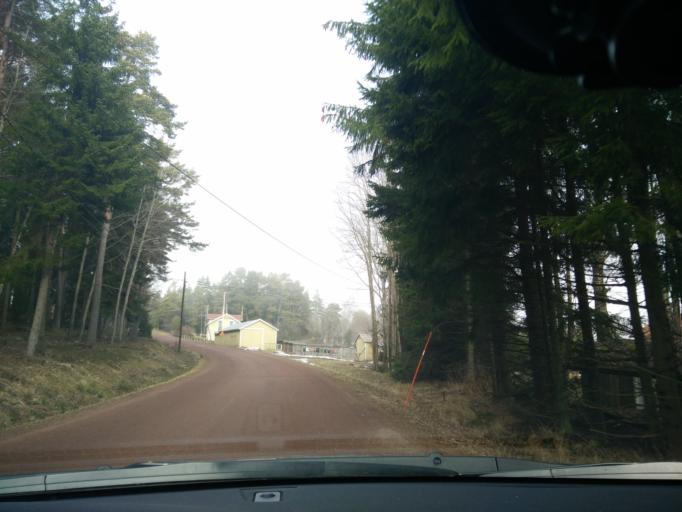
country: AX
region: Mariehamns stad
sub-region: Mariehamn
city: Mariehamn
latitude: 60.0950
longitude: 19.9141
